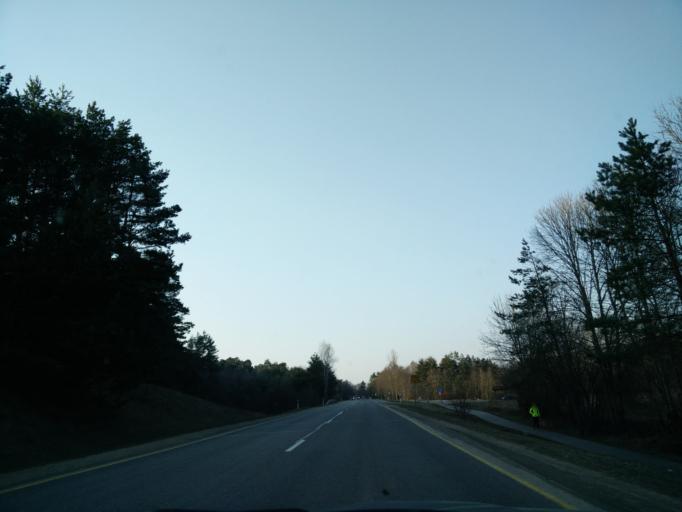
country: LT
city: Trakai
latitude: 54.6569
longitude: 24.9164
